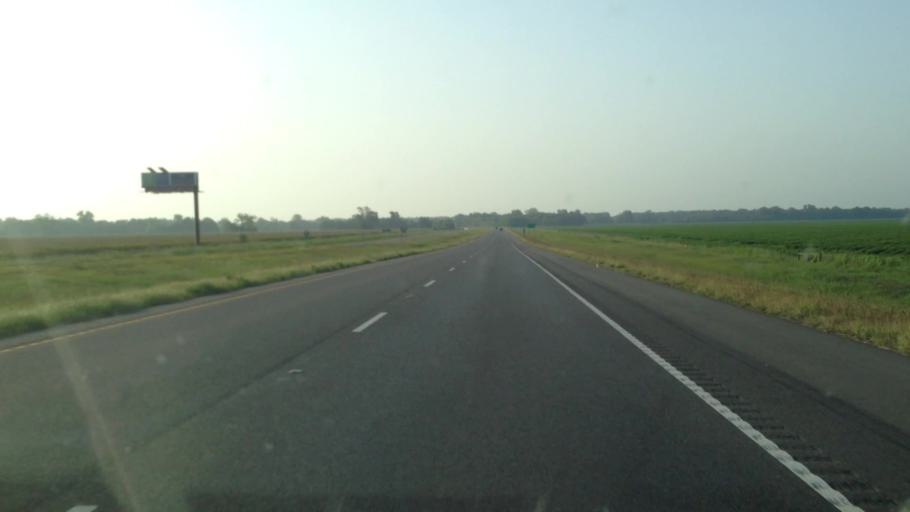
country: US
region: Louisiana
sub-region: Rapides Parish
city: Boyce
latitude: 31.3893
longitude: -92.6889
